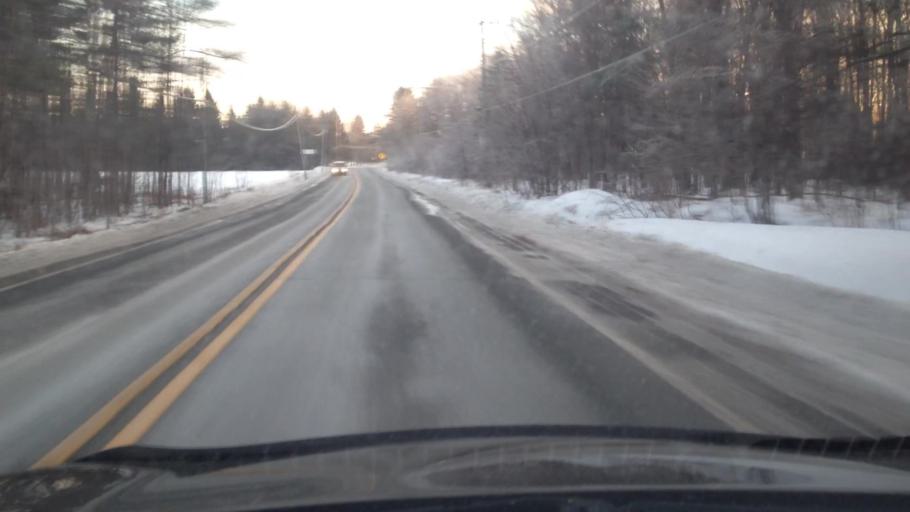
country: CA
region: Quebec
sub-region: Lanaudiere
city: Sainte-Julienne
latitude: 45.9191
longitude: -73.7388
